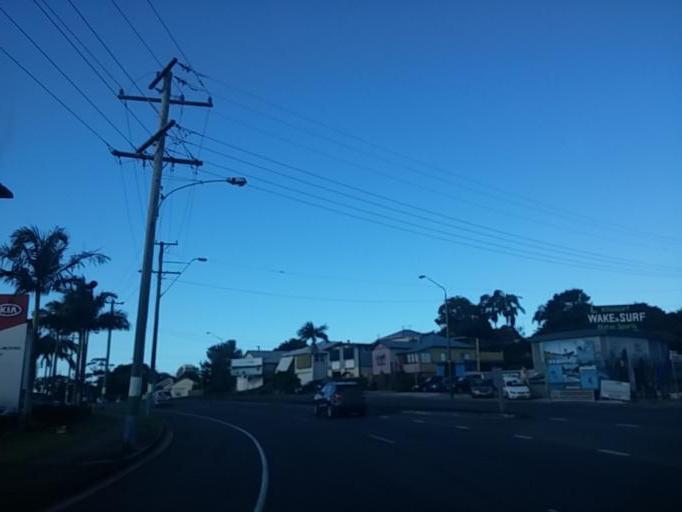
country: AU
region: New South Wales
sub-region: Tweed
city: Tweed Heads West
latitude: -28.1804
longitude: 153.5403
